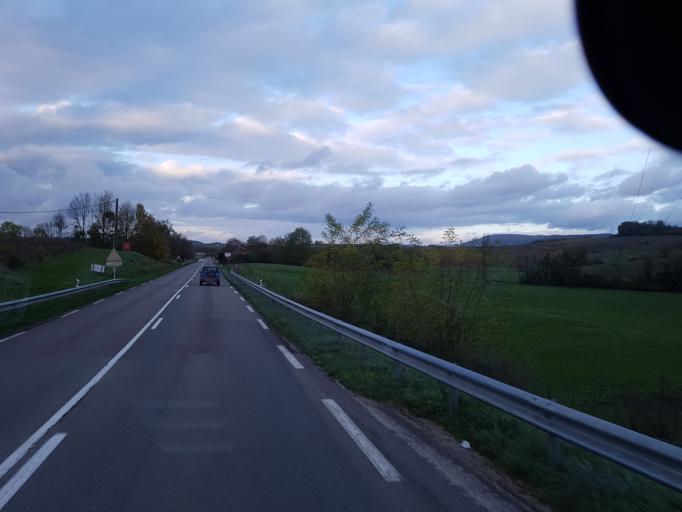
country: FR
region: Franche-Comte
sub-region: Departement du Jura
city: Arbois
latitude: 46.8873
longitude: 5.7288
